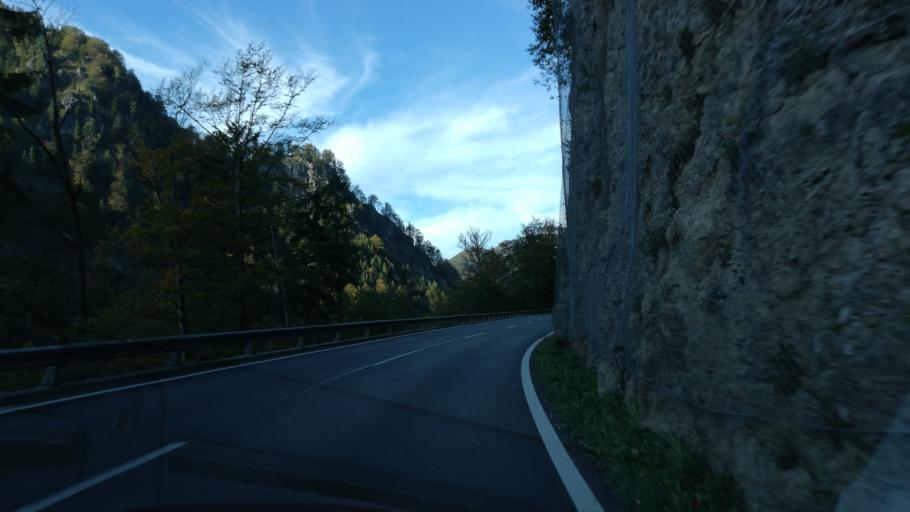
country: AT
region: Styria
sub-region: Politischer Bezirk Liezen
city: Altenmarkt bei Sankt Gallen
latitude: 47.7643
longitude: 14.6471
